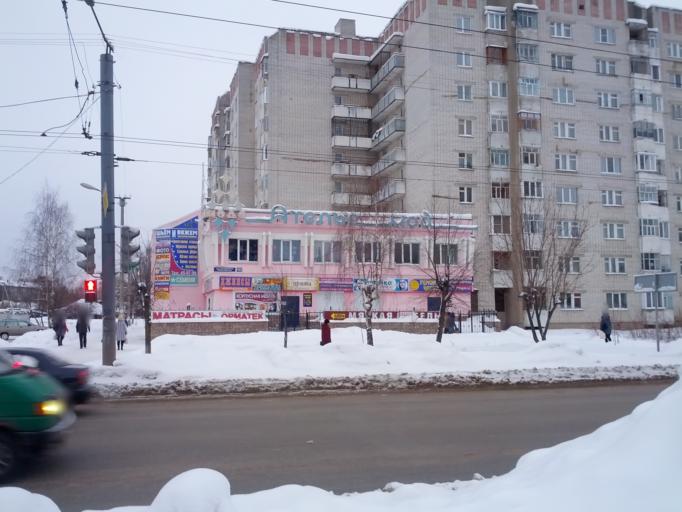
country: RU
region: Mariy-El
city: Yoshkar-Ola
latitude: 56.6464
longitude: 47.8645
